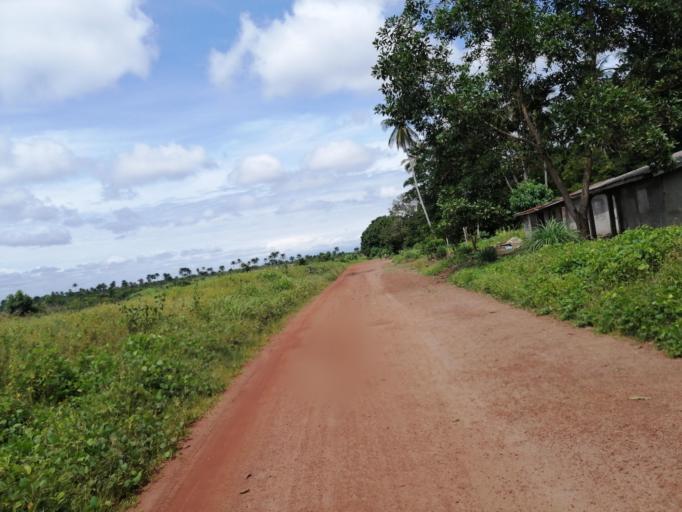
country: SL
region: Northern Province
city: Pepel
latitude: 8.6560
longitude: -13.0062
